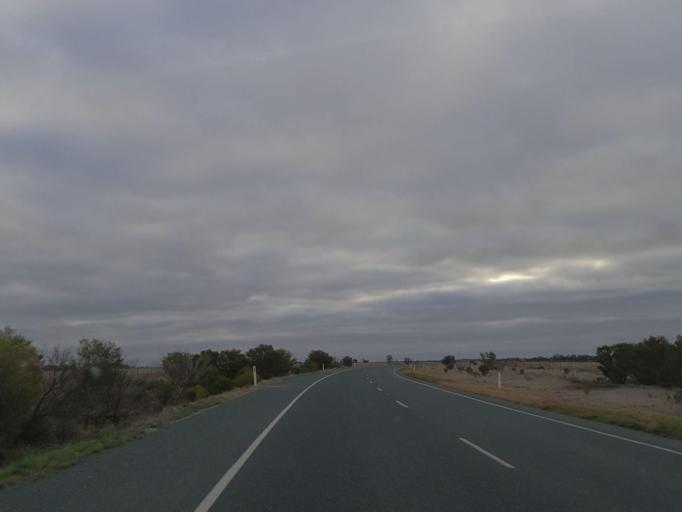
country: AU
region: Victoria
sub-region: Swan Hill
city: Swan Hill
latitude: -35.6267
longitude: 143.8099
